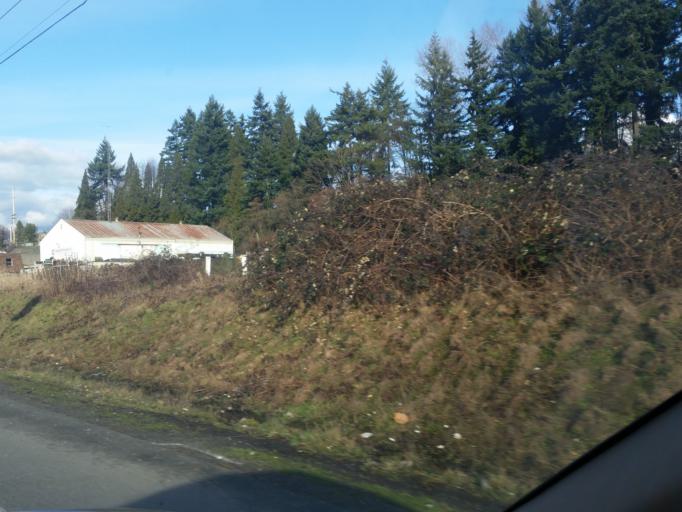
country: US
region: Washington
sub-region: King County
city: Woodinville
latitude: 47.7667
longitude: -122.1544
